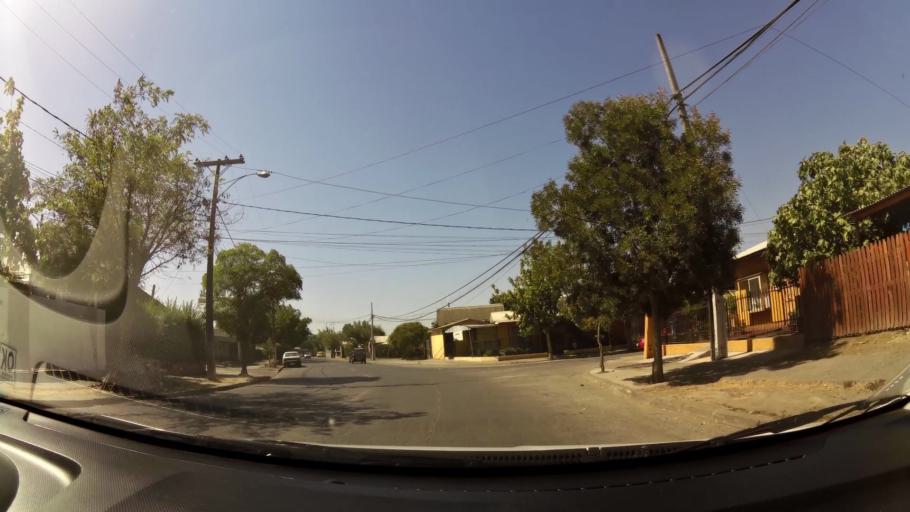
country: CL
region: Maule
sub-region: Provincia de Talca
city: Talca
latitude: -35.4414
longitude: -71.6629
